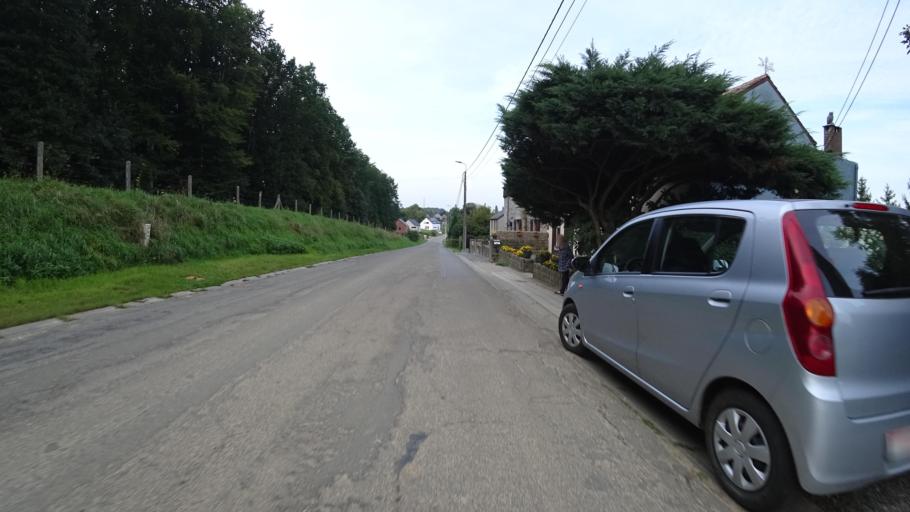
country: BE
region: Wallonia
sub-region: Province de Namur
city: Namur
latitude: 50.4995
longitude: 4.8651
